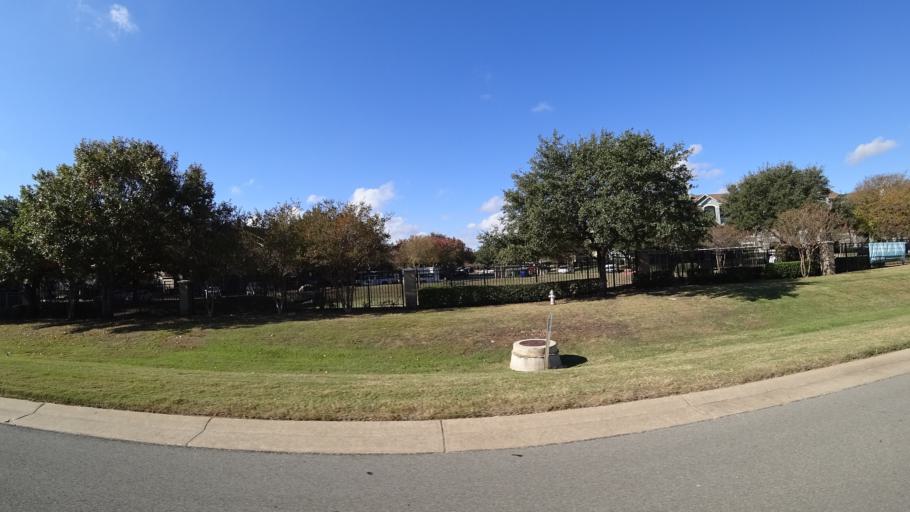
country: US
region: Texas
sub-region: Williamson County
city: Brushy Creek
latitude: 30.4867
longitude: -97.7710
